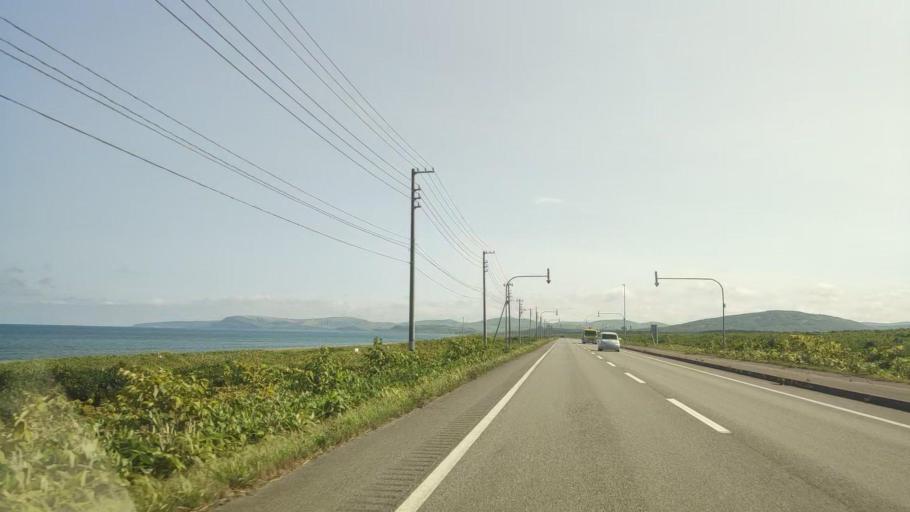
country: JP
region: Hokkaido
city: Makubetsu
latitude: 45.4149
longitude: 141.8252
